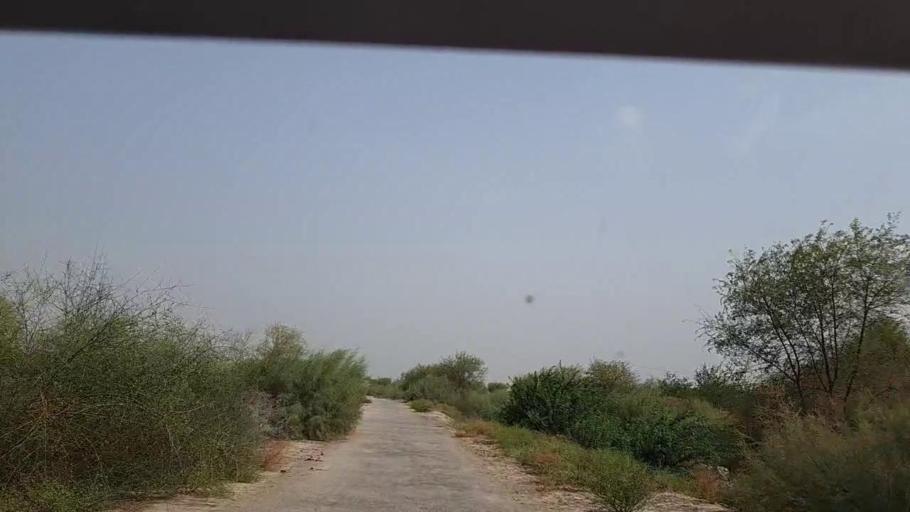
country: PK
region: Sindh
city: Khairpur Nathan Shah
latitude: 27.0299
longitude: 67.6743
